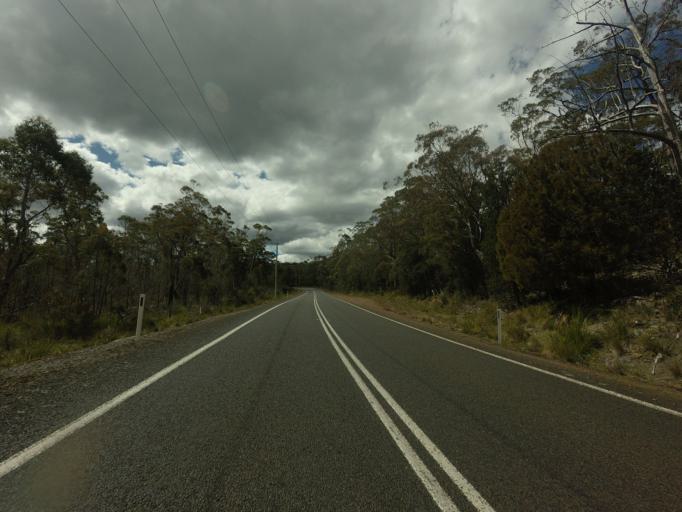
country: AU
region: Tasmania
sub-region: Northern Midlands
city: Evandale
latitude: -42.0045
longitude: 147.7231
